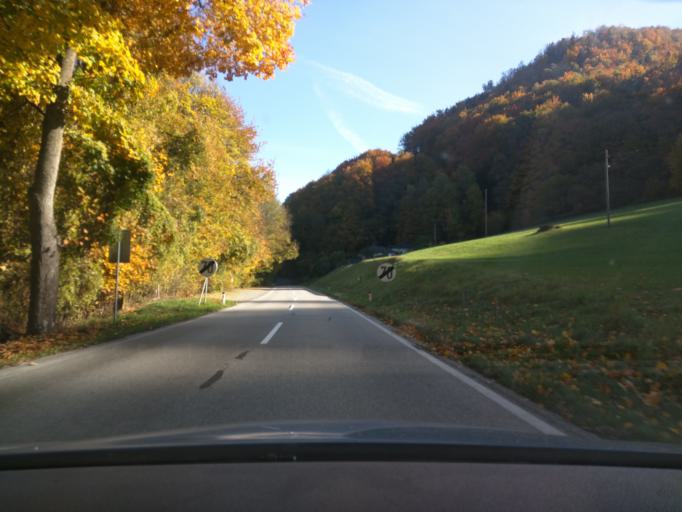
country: DE
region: Bavaria
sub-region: Lower Bavaria
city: Untergriesbach
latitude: 48.5148
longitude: 13.7109
